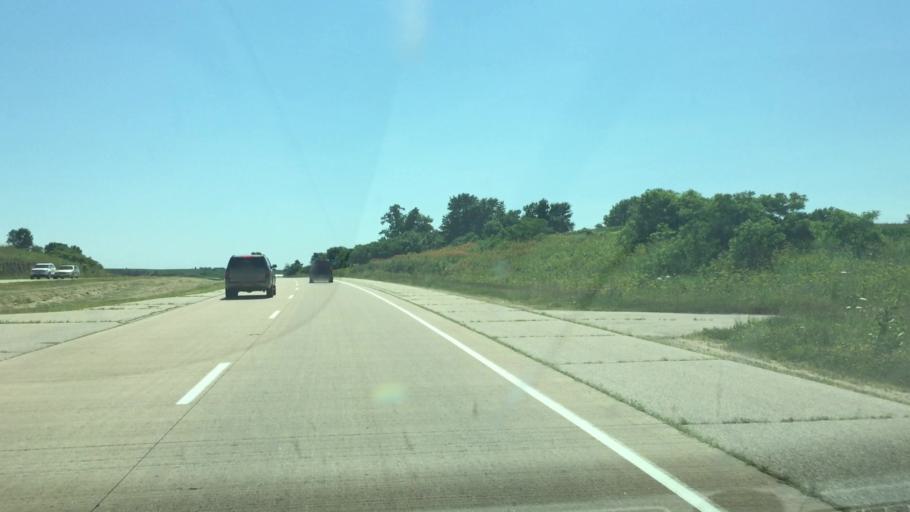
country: US
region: Wisconsin
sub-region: Iowa County
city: Mineral Point
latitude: 42.7886
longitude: -90.2971
